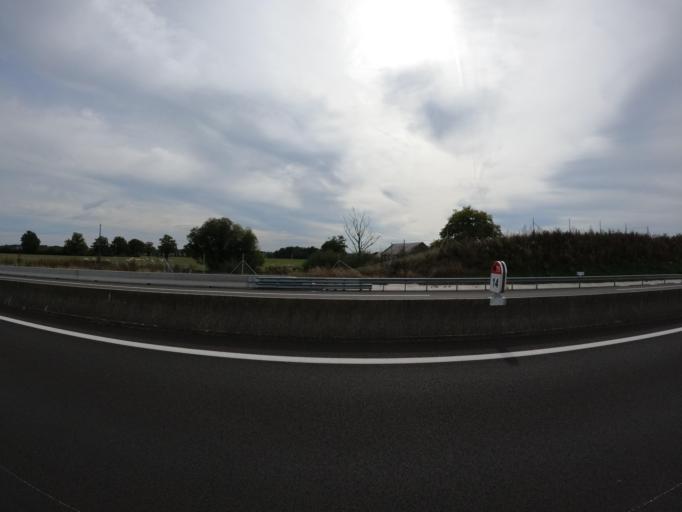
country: FR
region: Auvergne
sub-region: Departement de l'Allier
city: Buxieres-les-Mines
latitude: 46.4071
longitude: 3.0791
